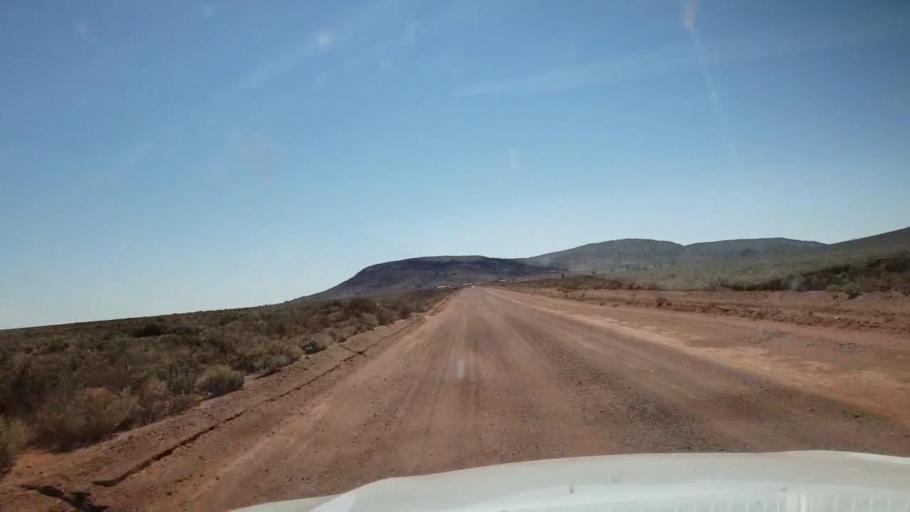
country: AU
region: South Australia
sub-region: Whyalla
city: Whyalla
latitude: -32.7023
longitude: 137.1355
